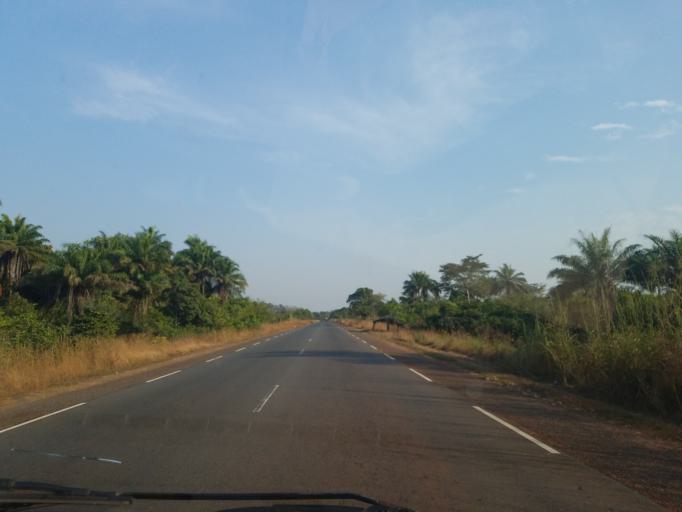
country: GN
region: Boke
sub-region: Boffa
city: Boffa
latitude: 10.3464
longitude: -14.2449
